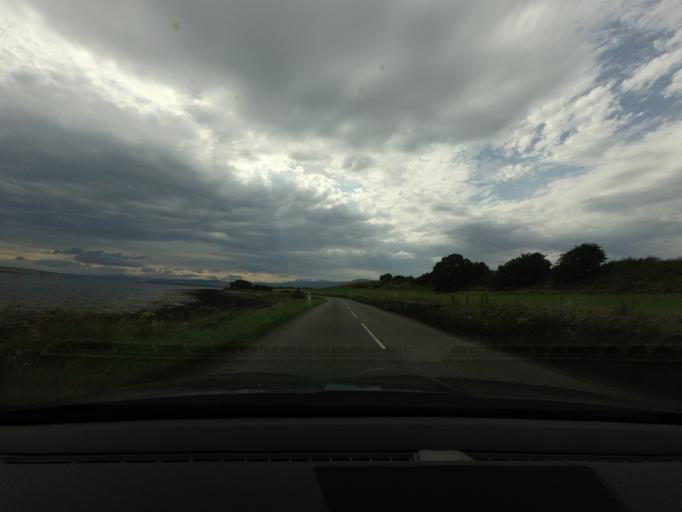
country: GB
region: Scotland
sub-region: Highland
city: Invergordon
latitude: 57.6927
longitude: -4.2064
